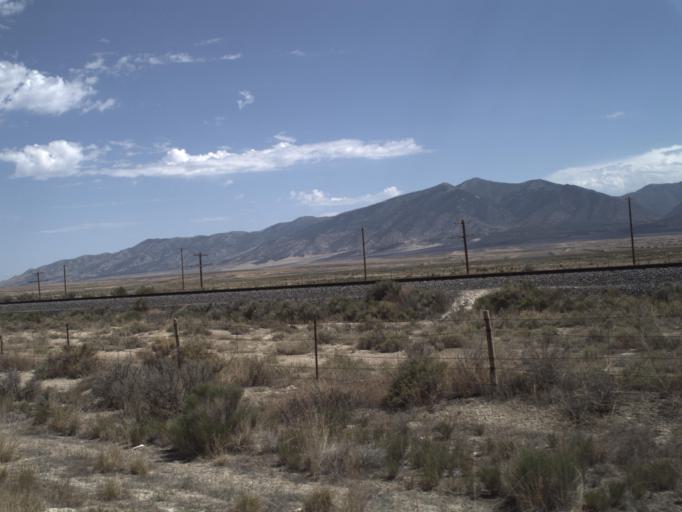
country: US
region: Utah
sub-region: Tooele County
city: Tooele
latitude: 40.2929
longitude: -112.4010
